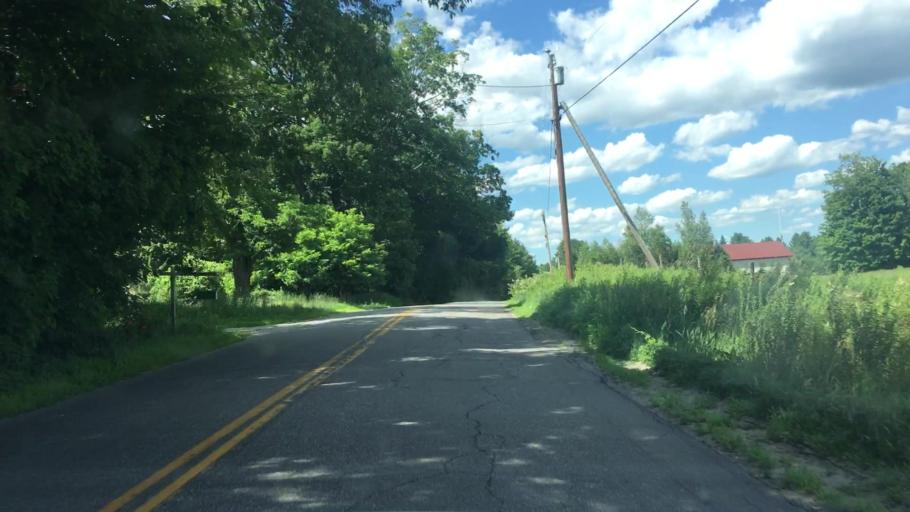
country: US
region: Maine
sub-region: Franklin County
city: Chesterville
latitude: 44.5768
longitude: -70.0903
